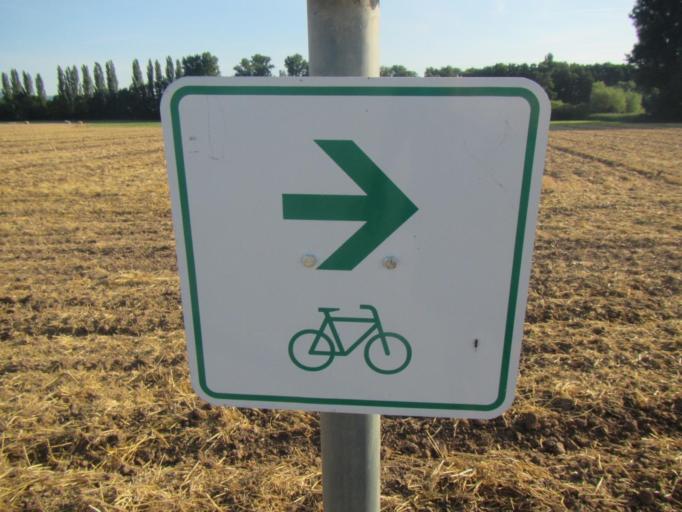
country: DE
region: Rheinland-Pfalz
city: Billigheim-Ingenheim
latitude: 49.1284
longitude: 8.1034
